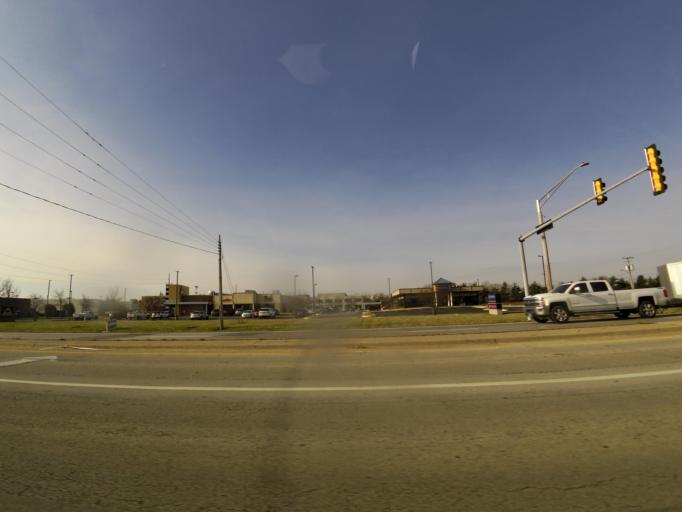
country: US
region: Illinois
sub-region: Macon County
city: Forsyth
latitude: 39.9234
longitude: -88.9553
